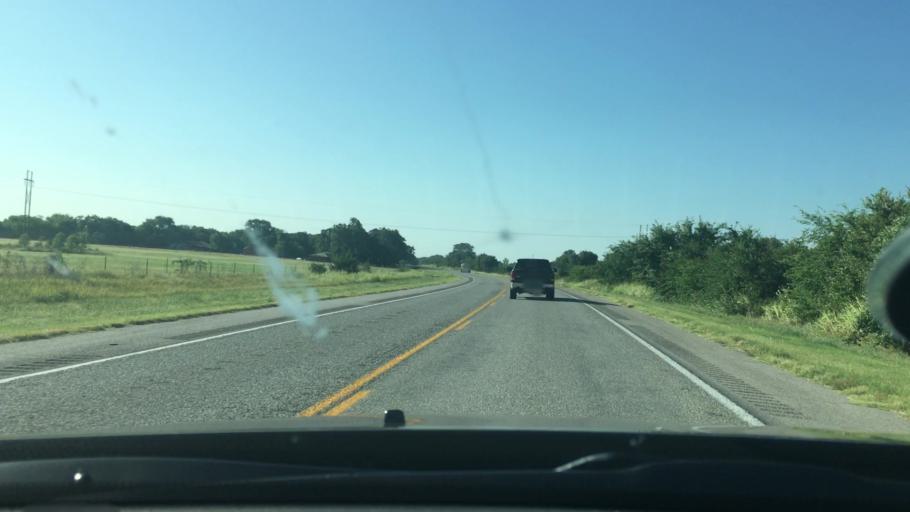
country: US
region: Oklahoma
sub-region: Johnston County
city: Tishomingo
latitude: 34.2633
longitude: -96.7712
